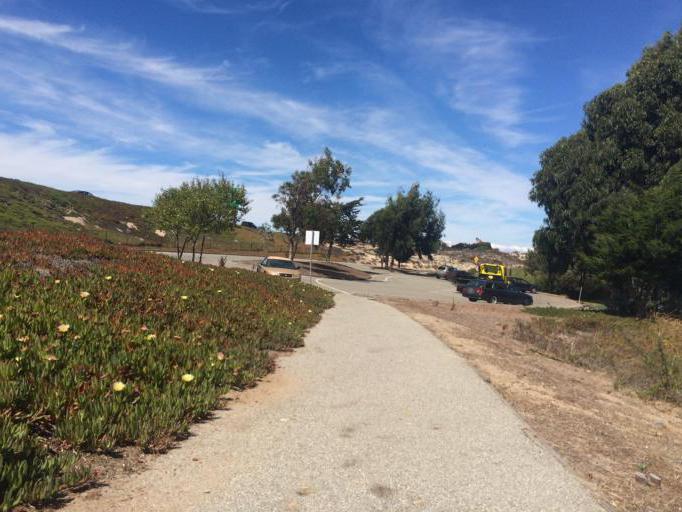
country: US
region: California
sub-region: Monterey County
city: Seaside
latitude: 36.6068
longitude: -121.8604
